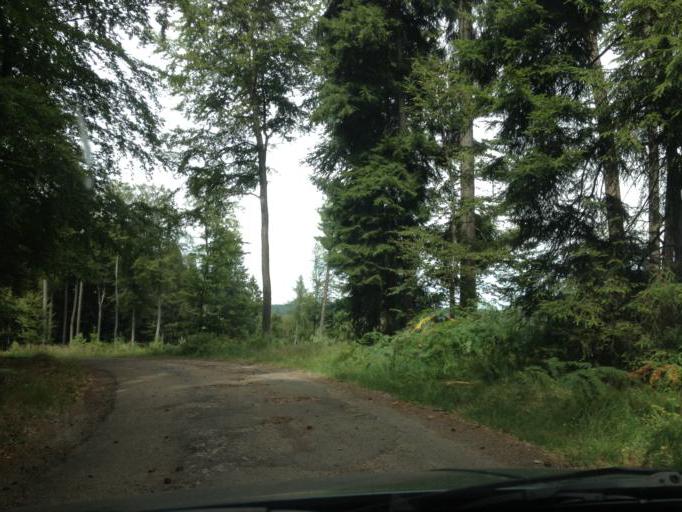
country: DE
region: Rheinland-Pfalz
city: Wilgartswiesen
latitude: 49.2884
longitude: 7.8982
